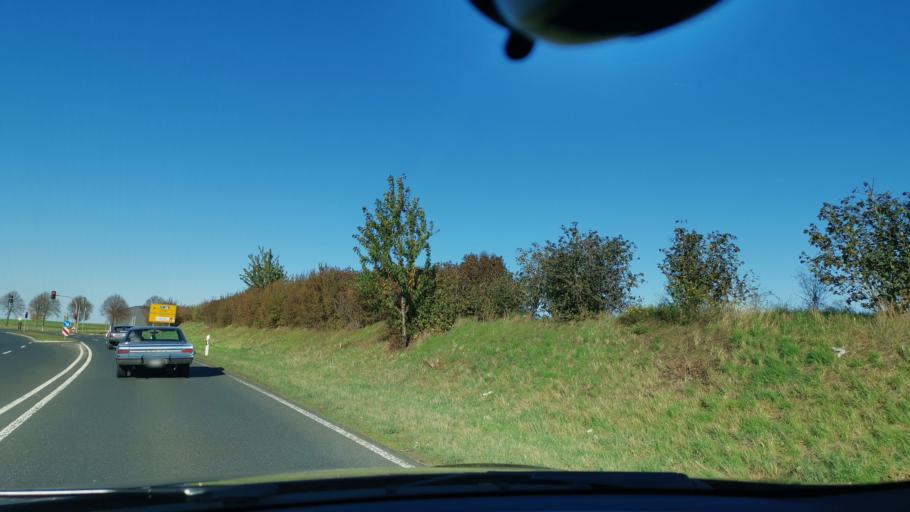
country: DE
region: North Rhine-Westphalia
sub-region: Regierungsbezirk Dusseldorf
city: Rommerskirchen
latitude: 51.0362
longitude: 6.6748
